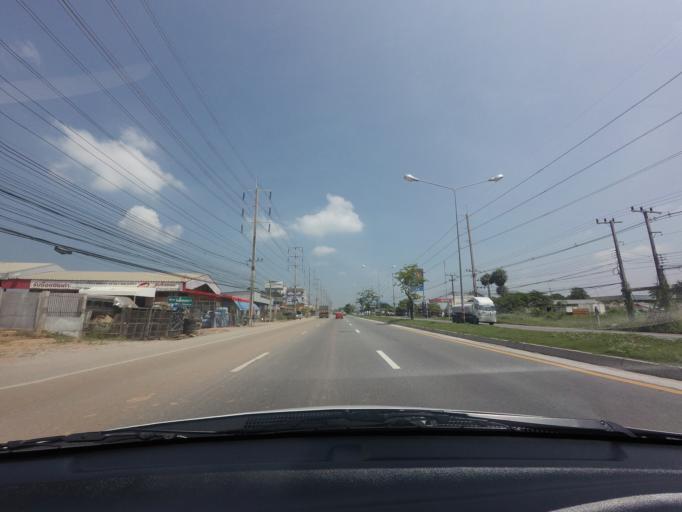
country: TH
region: Chachoengsao
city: Chachoengsao
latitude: 13.6424
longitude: 101.0433
